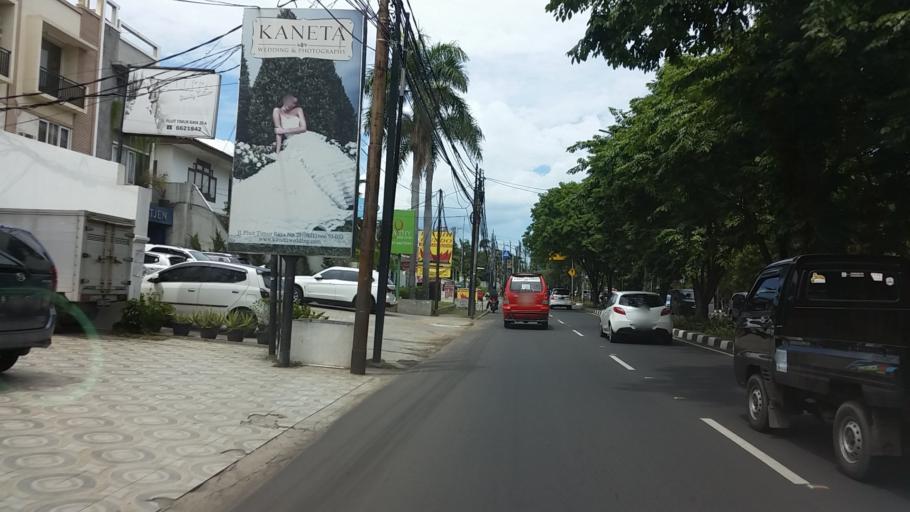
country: ID
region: Jakarta Raya
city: Jakarta
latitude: -6.1200
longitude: 106.7941
